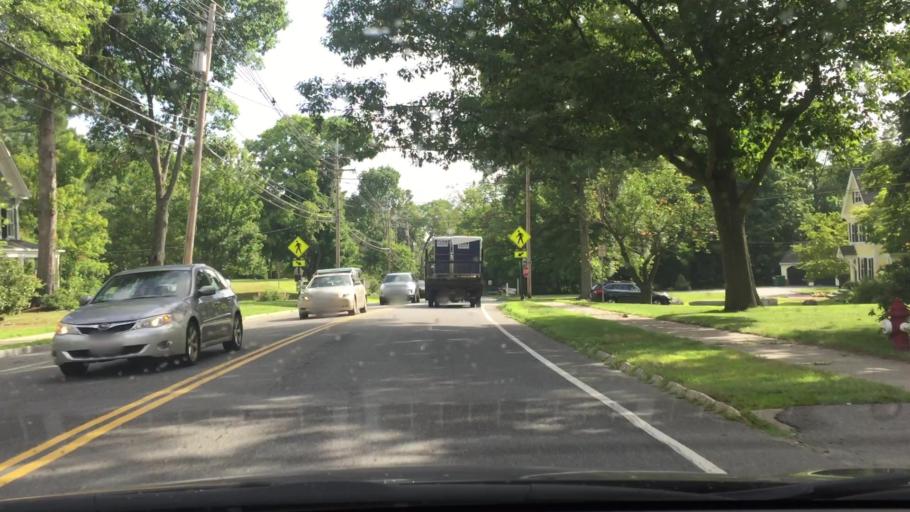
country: US
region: Massachusetts
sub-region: Middlesex County
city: Acton
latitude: 42.4870
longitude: -71.4318
